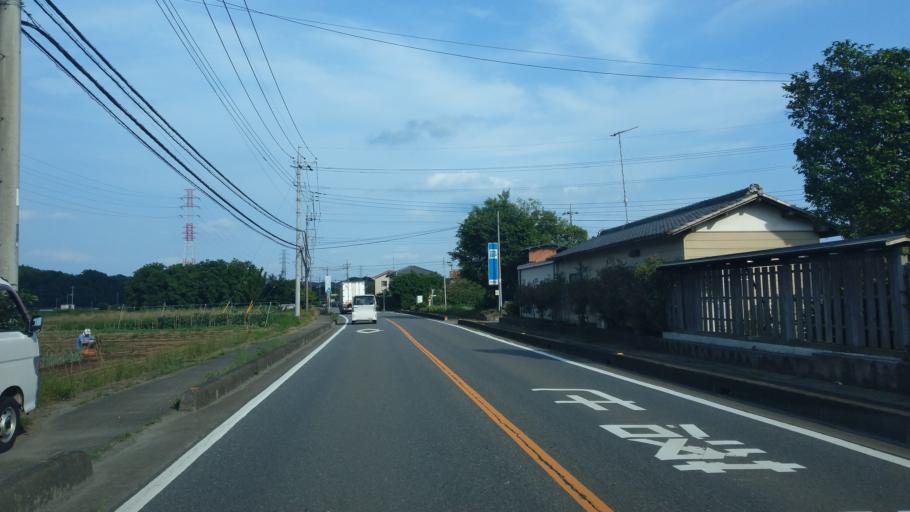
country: JP
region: Saitama
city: Ogawa
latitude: 36.0932
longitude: 139.2767
